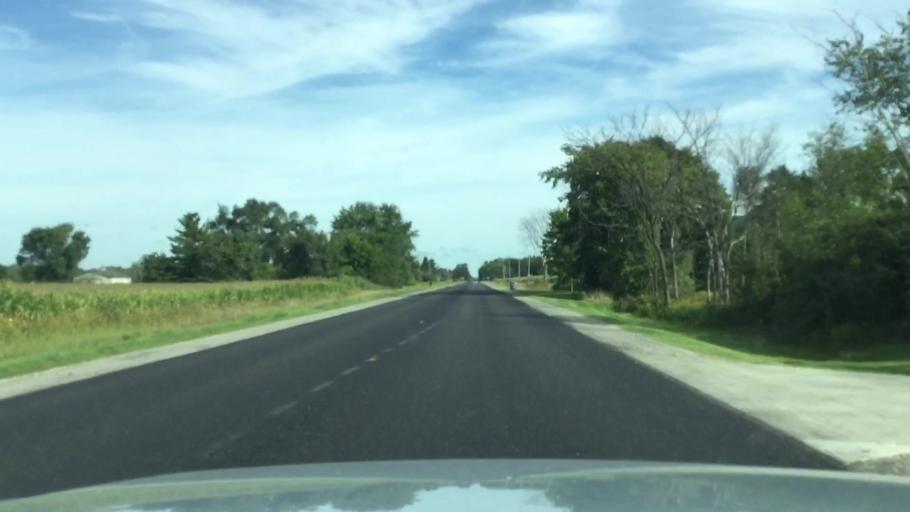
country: US
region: Michigan
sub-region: Genesee County
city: Montrose
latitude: 43.1406
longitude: -83.9294
